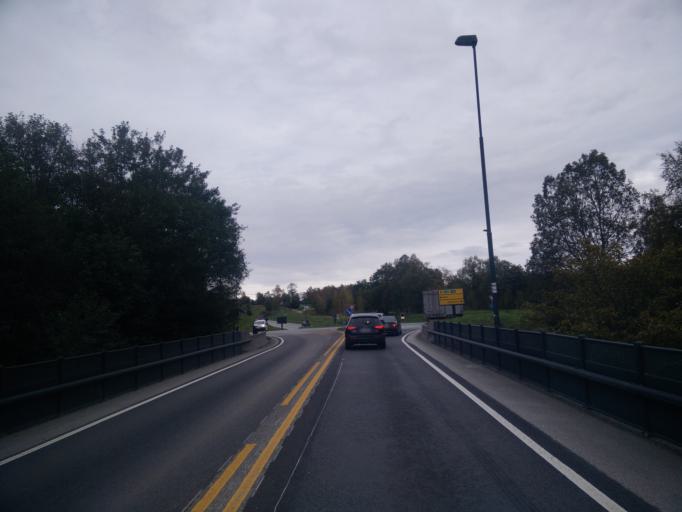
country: NO
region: More og Romsdal
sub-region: Haram
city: Brattvag
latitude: 62.4603
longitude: 6.3578
